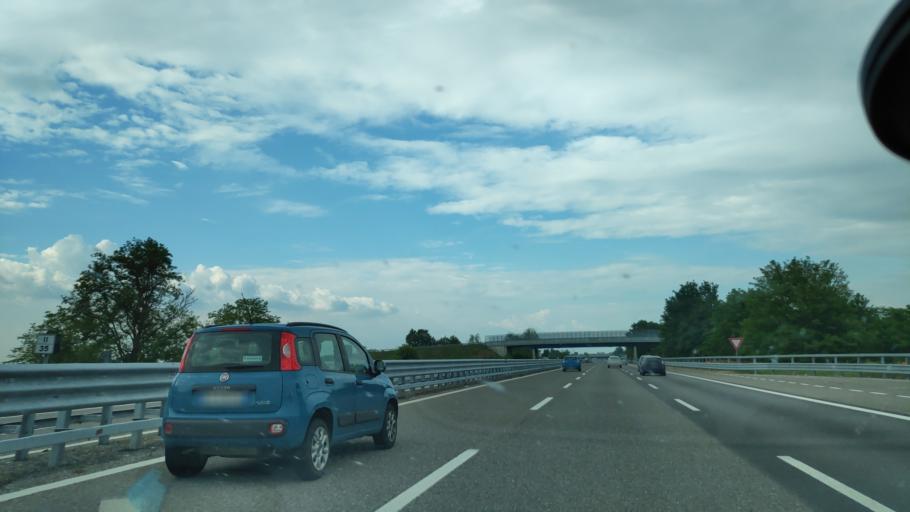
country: IT
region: Lombardy
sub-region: Provincia di Pavia
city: Pieve Albignola
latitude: 45.1356
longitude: 8.9839
